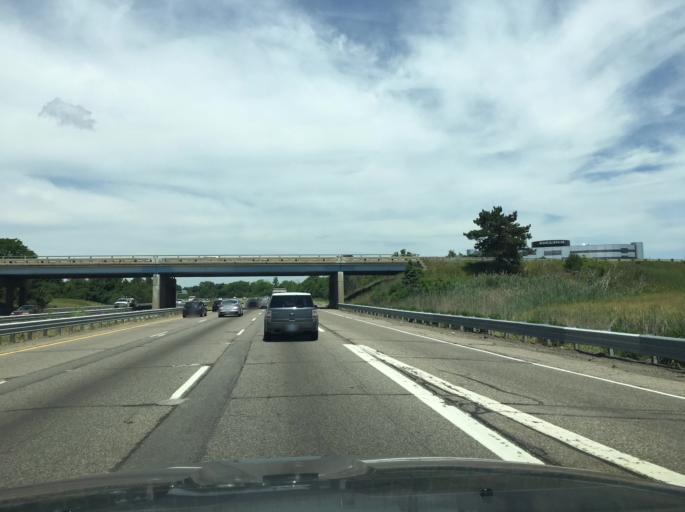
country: US
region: Michigan
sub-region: Oakland County
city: Troy
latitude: 42.5989
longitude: -83.1621
